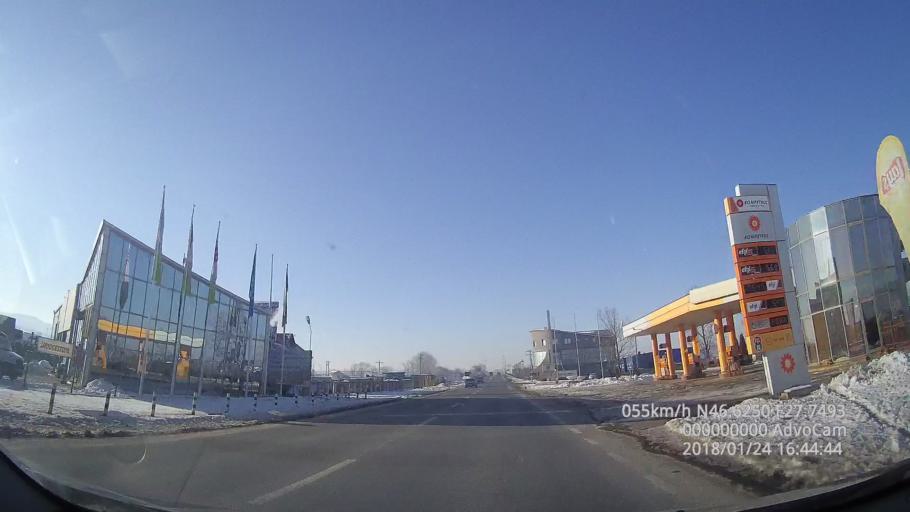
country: RO
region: Vaslui
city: Vaslui
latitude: 46.6250
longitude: 27.7487
